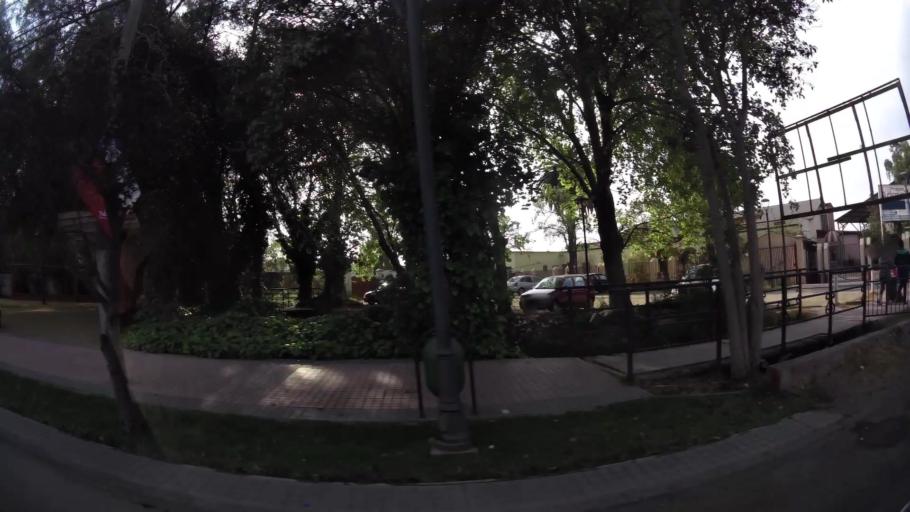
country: CL
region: Santiago Metropolitan
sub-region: Provincia de Talagante
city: Talagante
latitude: -33.6724
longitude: -70.9253
